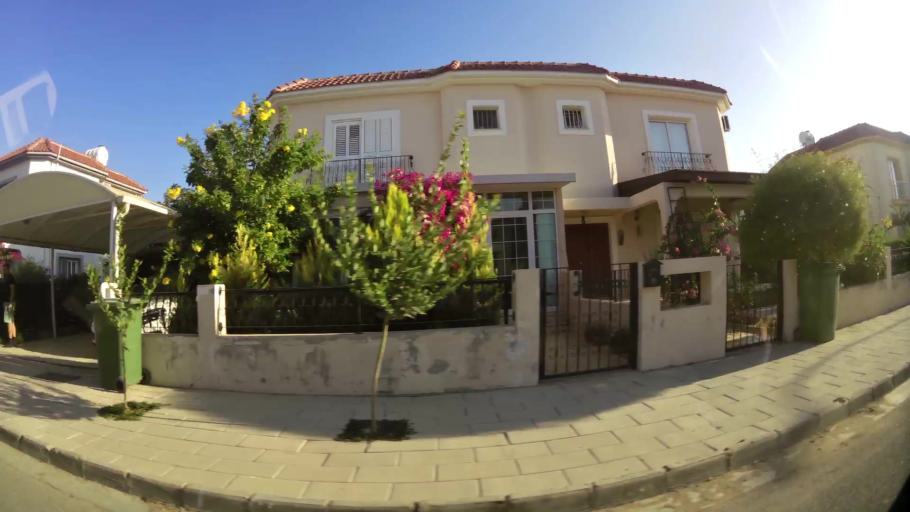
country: CY
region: Lefkosia
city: Nicosia
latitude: 35.2064
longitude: 33.2970
